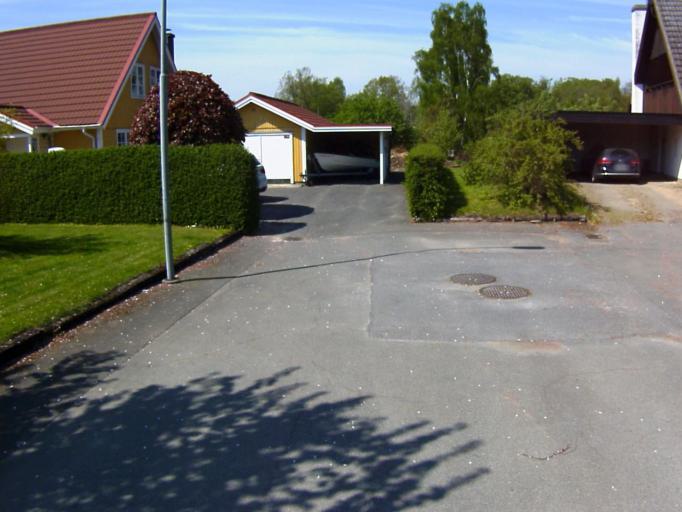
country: SE
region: Skane
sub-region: Kristianstads Kommun
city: Tollarp
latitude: 56.1680
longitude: 14.2908
